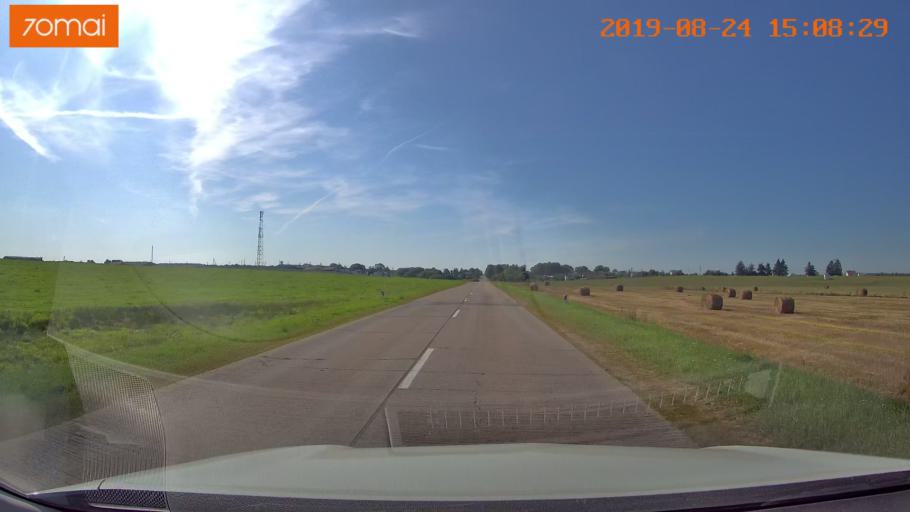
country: BY
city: Michanovichi
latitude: 53.6084
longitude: 27.6562
